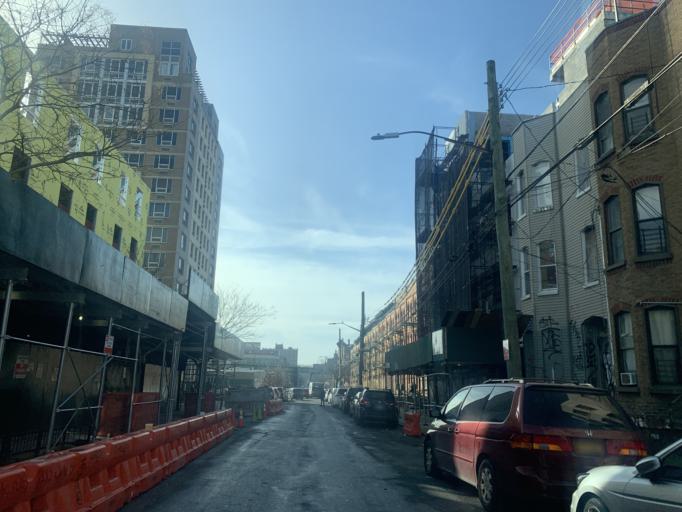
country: US
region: New York
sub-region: Kings County
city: East New York
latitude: 40.7006
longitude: -73.9136
